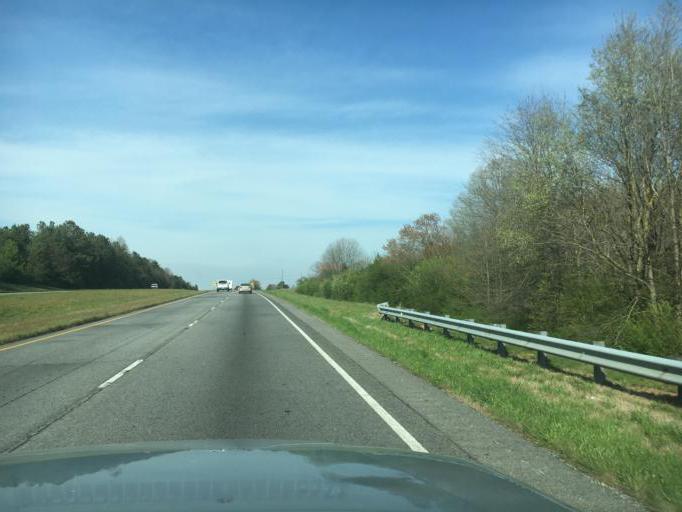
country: US
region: Georgia
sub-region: Habersham County
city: Raoul
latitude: 34.4548
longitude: -83.6113
